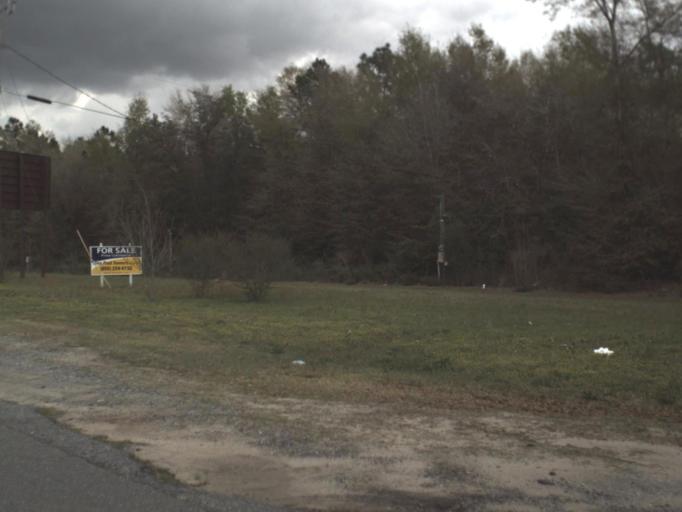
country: US
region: Florida
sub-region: Okaloosa County
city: Crestview
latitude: 30.7169
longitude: -86.5695
